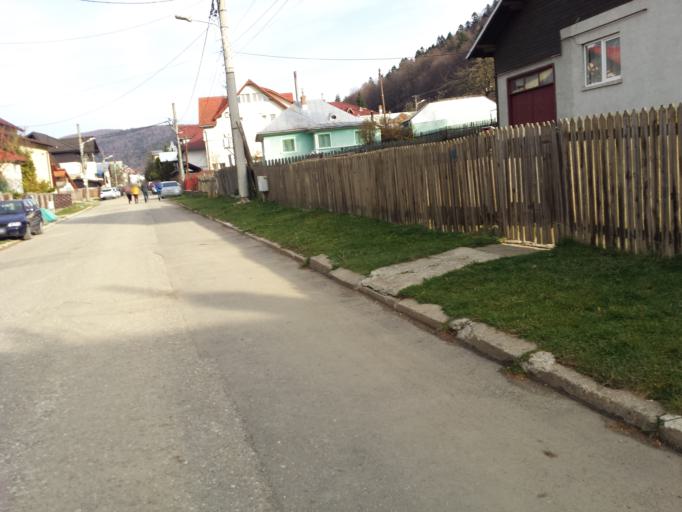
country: RO
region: Prahova
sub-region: Oras Busteni
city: Busteni
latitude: 45.4066
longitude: 25.5404
